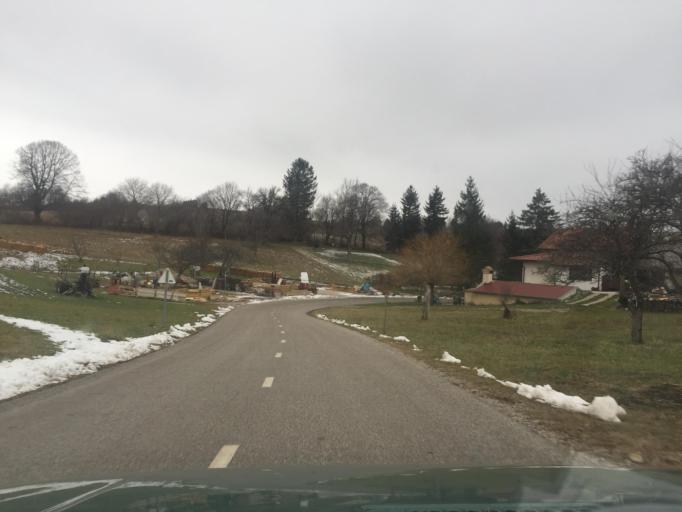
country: SI
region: Kanal
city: Kanal
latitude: 46.0550
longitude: 13.6894
